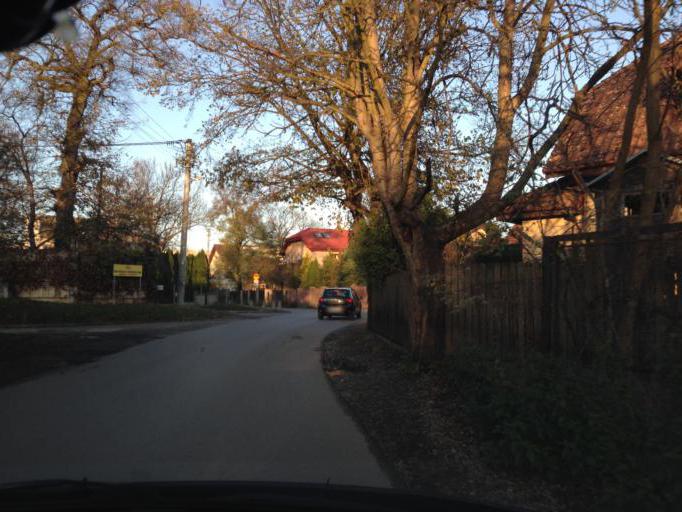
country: PL
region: Lesser Poland Voivodeship
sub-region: Powiat krakowski
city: Rzaska
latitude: 50.0755
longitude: 19.8786
